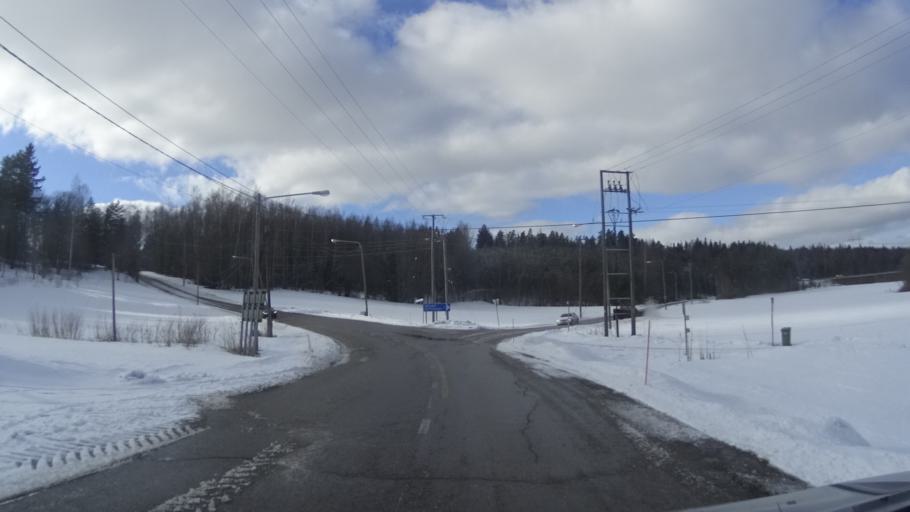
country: FI
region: Uusimaa
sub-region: Helsinki
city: Vantaa
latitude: 60.2579
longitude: 25.1461
